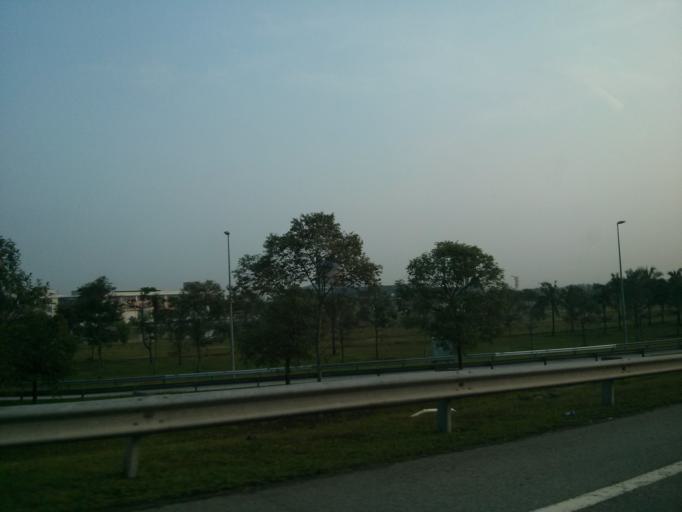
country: MY
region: Negeri Sembilan
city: Kampung Baharu Nilai
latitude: 2.7835
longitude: 101.6749
